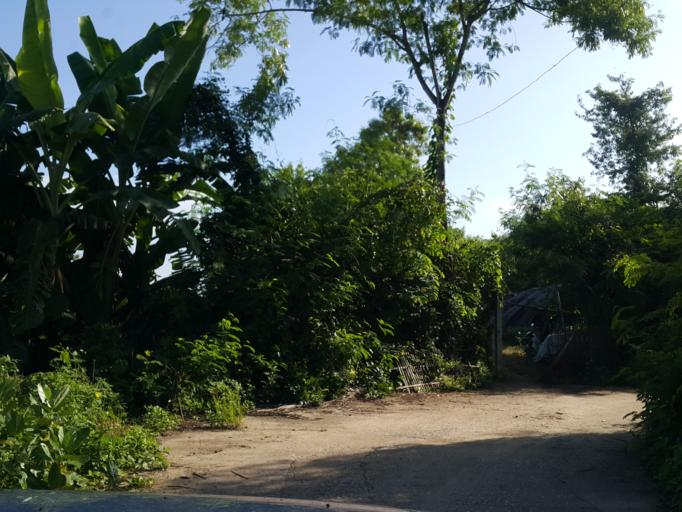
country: TH
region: Chiang Mai
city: San Kamphaeng
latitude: 18.7884
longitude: 99.1035
